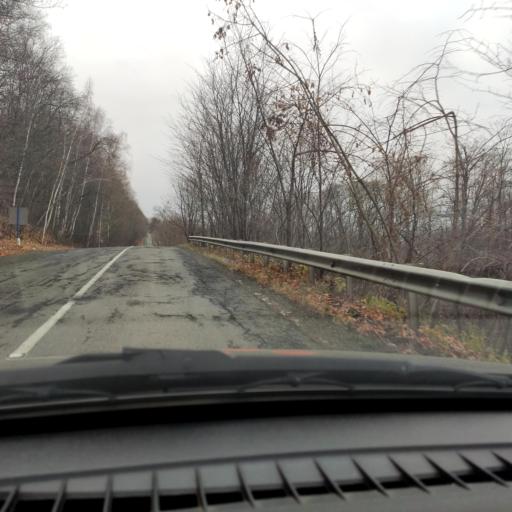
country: RU
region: Samara
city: Povolzhskiy
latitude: 53.4388
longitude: 49.6989
